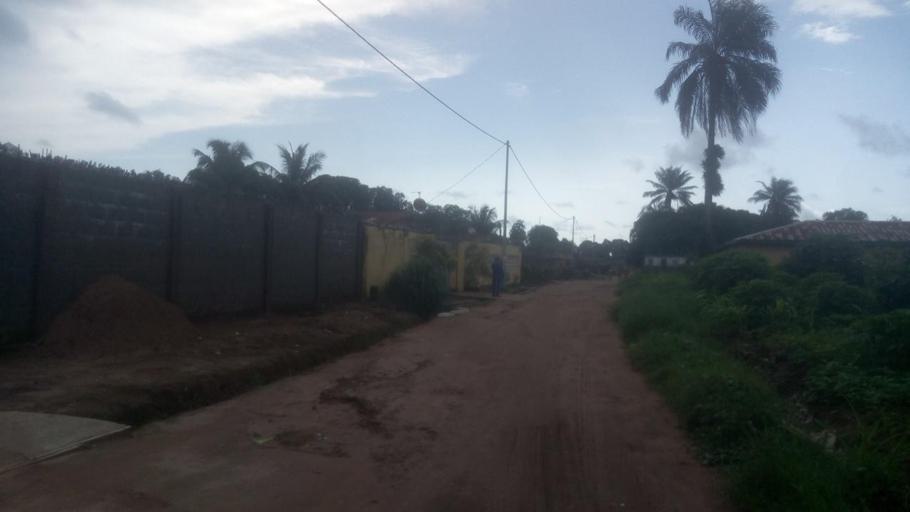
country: SL
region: Northern Province
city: Masoyila
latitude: 8.6064
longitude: -13.1868
